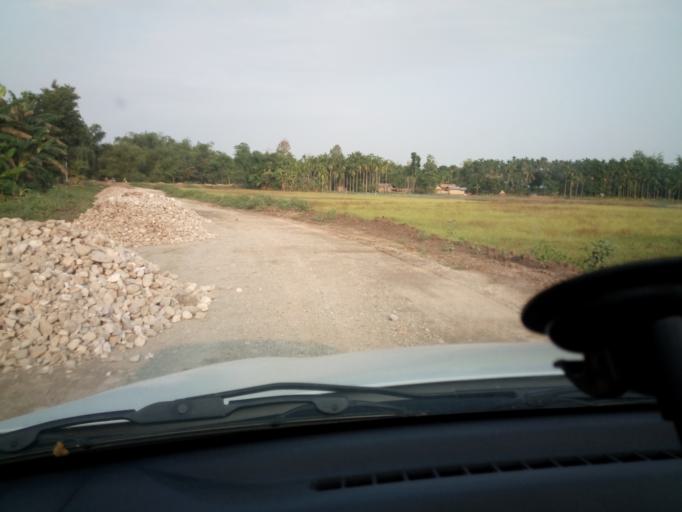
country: IN
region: Assam
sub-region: Udalguri
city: Udalguri
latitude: 26.7029
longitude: 92.0873
